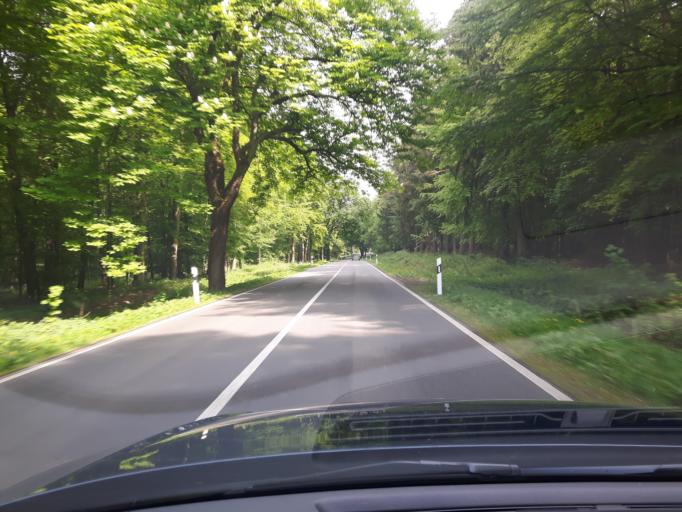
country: DE
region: Mecklenburg-Vorpommern
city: Gross Wokern
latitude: 53.6244
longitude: 12.4680
